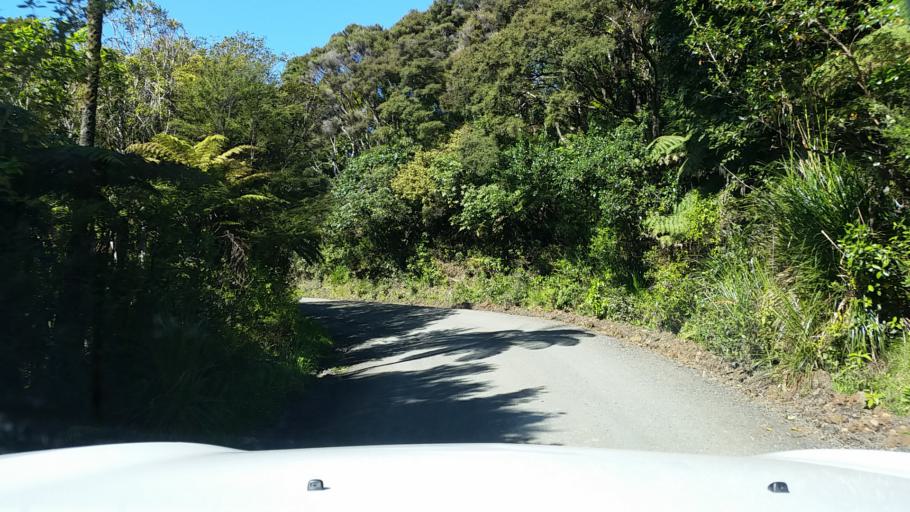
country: NZ
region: Auckland
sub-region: Auckland
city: Titirangi
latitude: -37.0218
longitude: 174.5379
